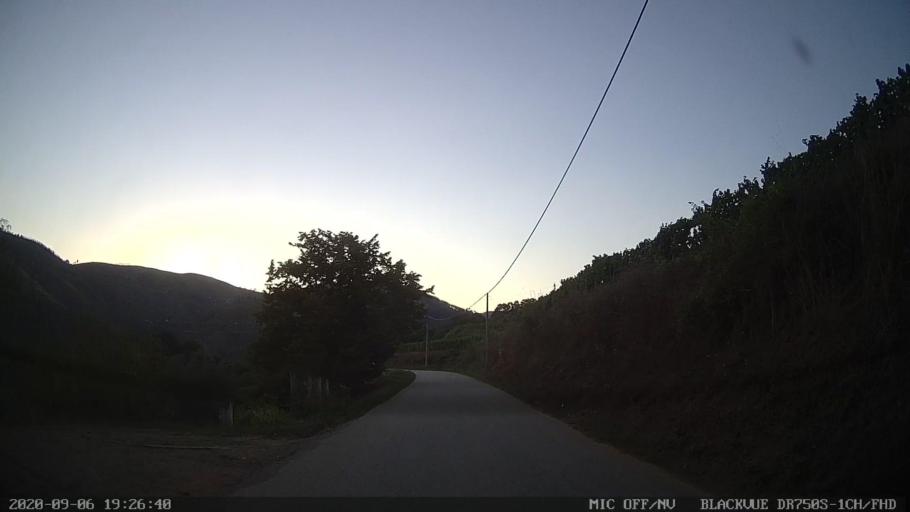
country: PT
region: Vila Real
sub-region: Mesao Frio
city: Mesao Frio
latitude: 41.1814
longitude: -7.9160
